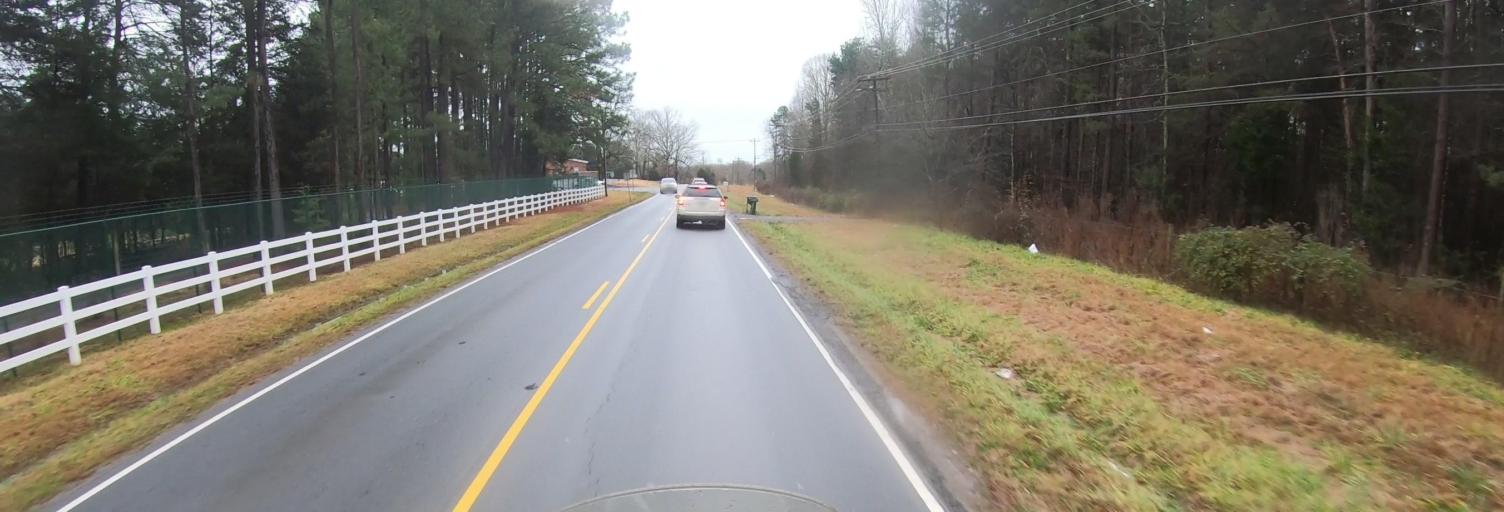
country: US
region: South Carolina
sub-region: York County
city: Lake Wylie
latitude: 35.0847
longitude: -81.0046
